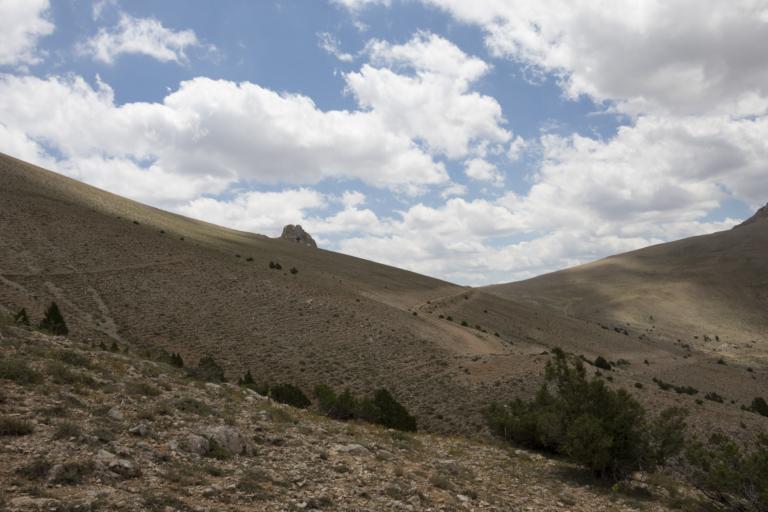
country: TR
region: Kayseri
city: Toklar
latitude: 38.3188
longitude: 36.0958
